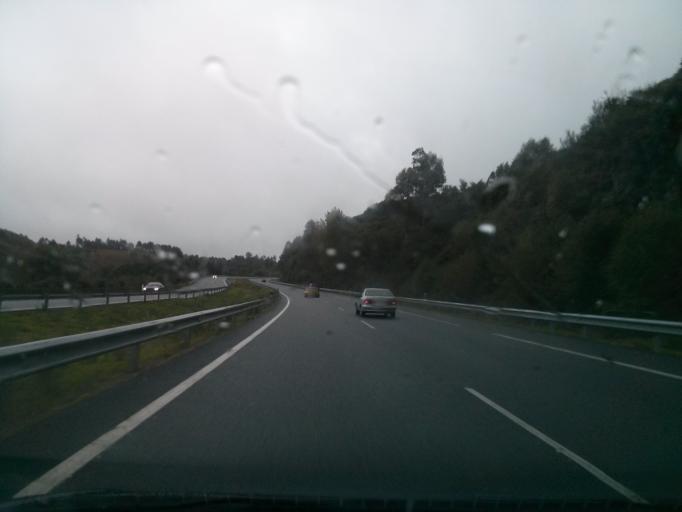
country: ES
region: Galicia
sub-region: Provincia de Ourense
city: Melon
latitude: 42.2423
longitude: -8.2280
